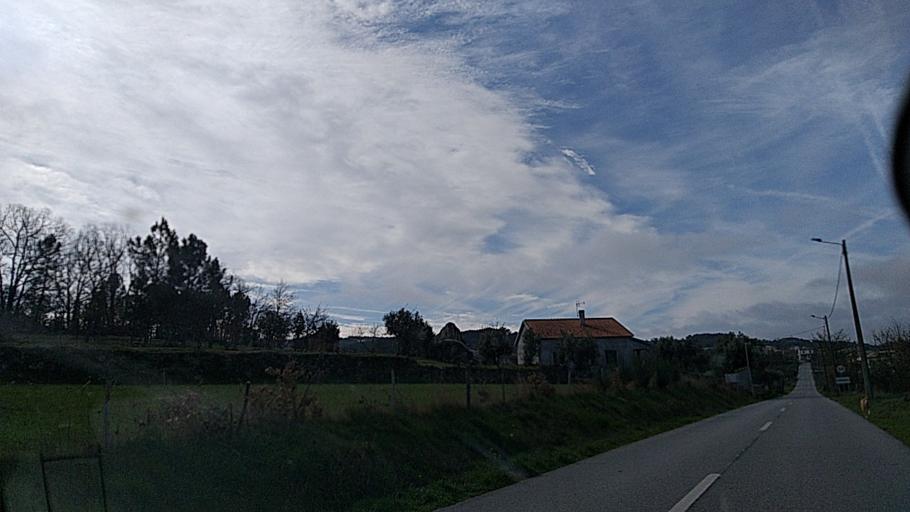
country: PT
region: Guarda
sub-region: Fornos de Algodres
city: Fornos de Algodres
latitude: 40.6619
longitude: -7.5311
